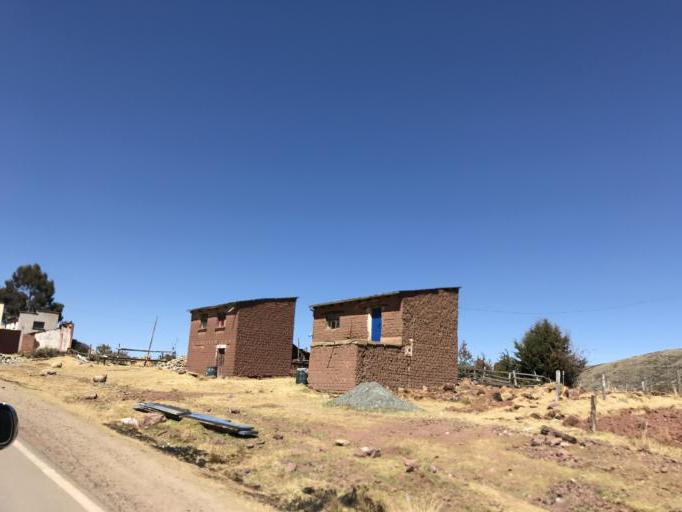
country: BO
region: La Paz
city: San Pablo
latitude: -16.2156
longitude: -68.8453
